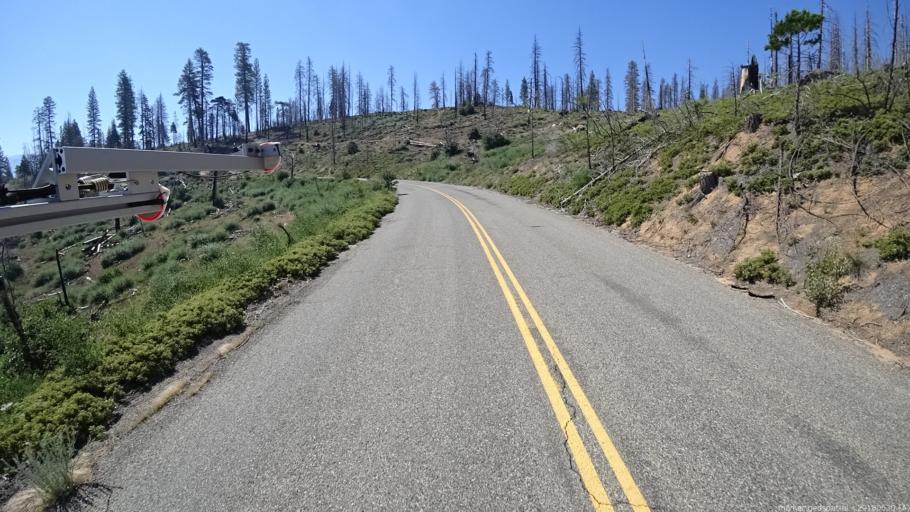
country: US
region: California
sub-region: Madera County
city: Oakhurst
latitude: 37.3373
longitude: -119.3721
